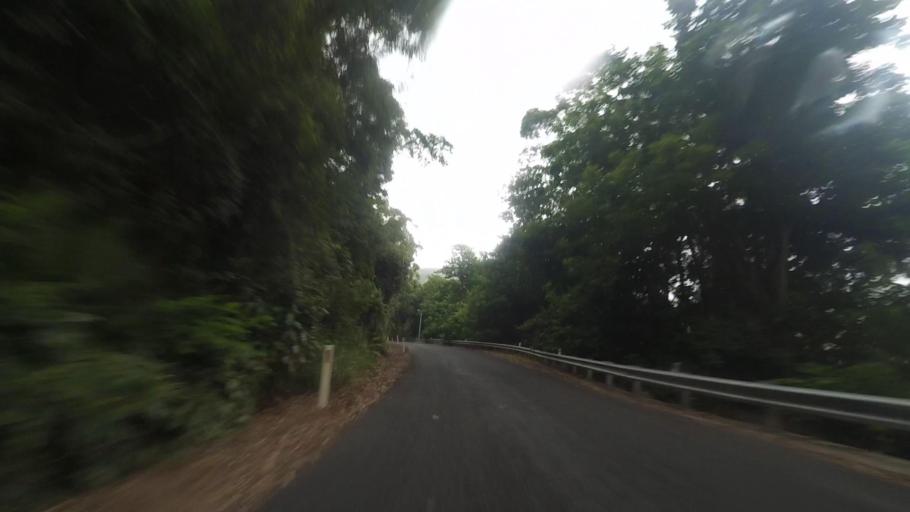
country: AU
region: New South Wales
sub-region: Wollongong
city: Cordeaux Heights
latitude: -34.4183
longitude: 150.8178
